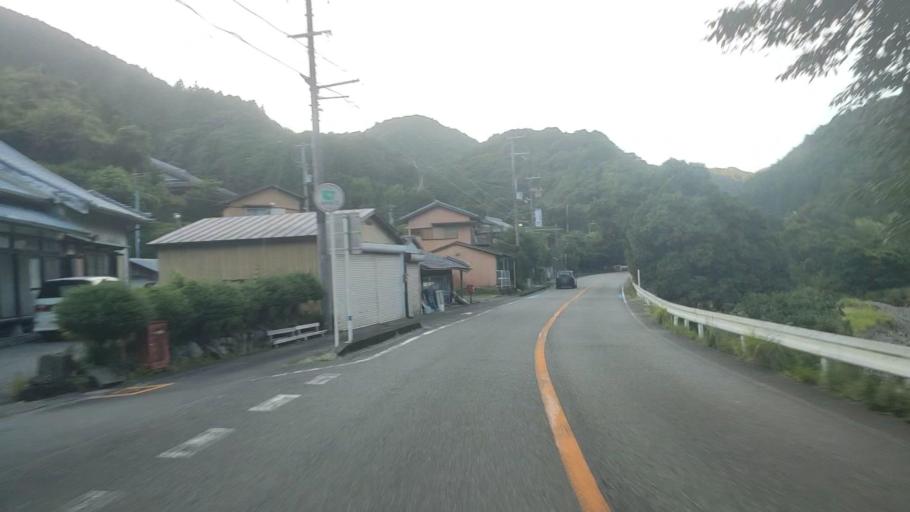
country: JP
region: Wakayama
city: Tanabe
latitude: 33.8132
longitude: 135.5502
